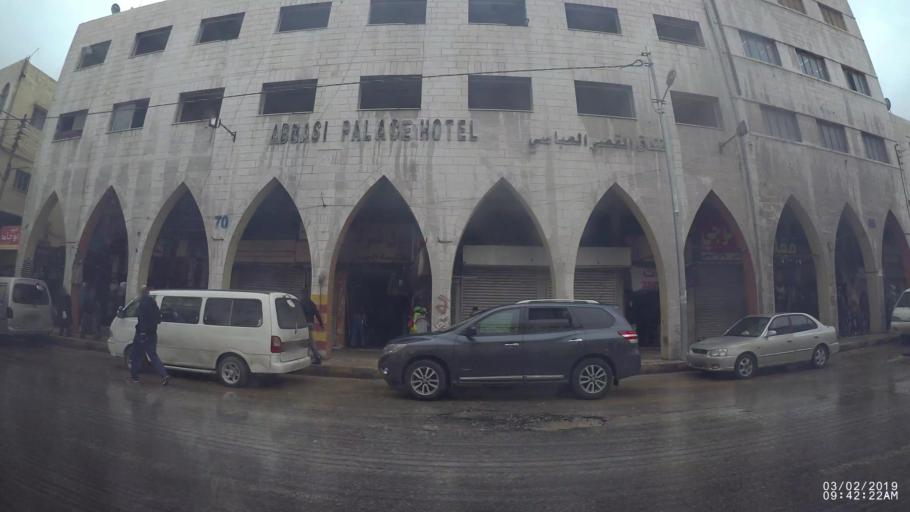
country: JO
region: Amman
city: Amman
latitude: 31.9475
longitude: 35.9344
